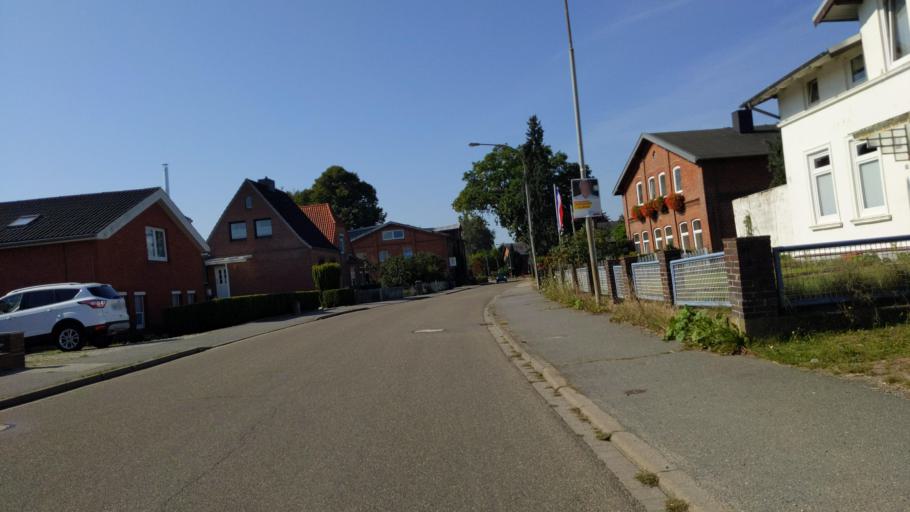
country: DE
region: Schleswig-Holstein
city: Stockelsdorf
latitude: 53.8798
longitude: 10.6204
